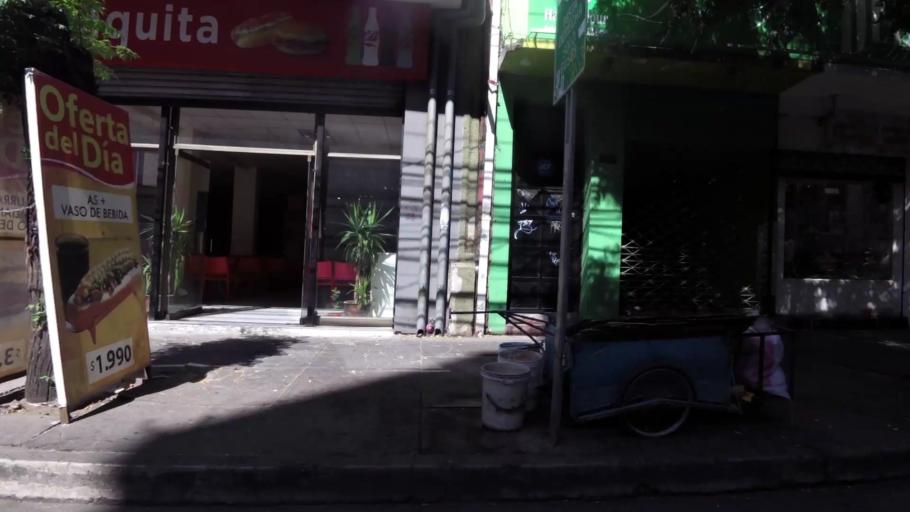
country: CL
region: Maule
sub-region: Provincia de Talca
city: Talca
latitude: -35.4284
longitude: -71.6599
